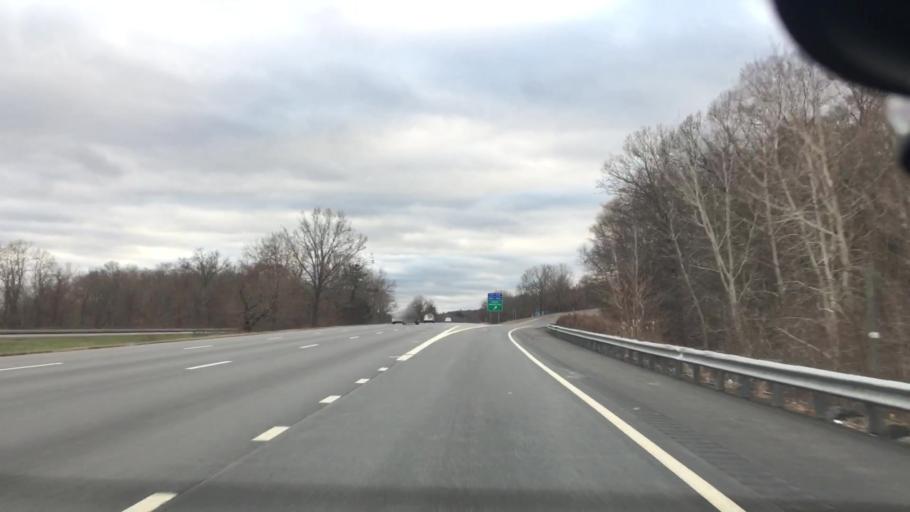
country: US
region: New York
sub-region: Westchester County
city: Bedford Hills
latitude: 41.2342
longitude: -73.6786
